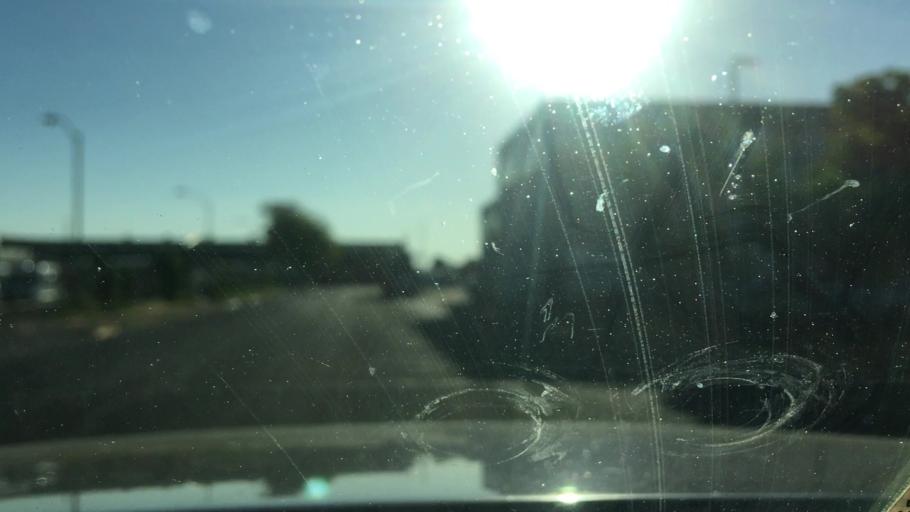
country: US
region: Oregon
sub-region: Lane County
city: Eugene
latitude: 44.0506
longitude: -123.1218
